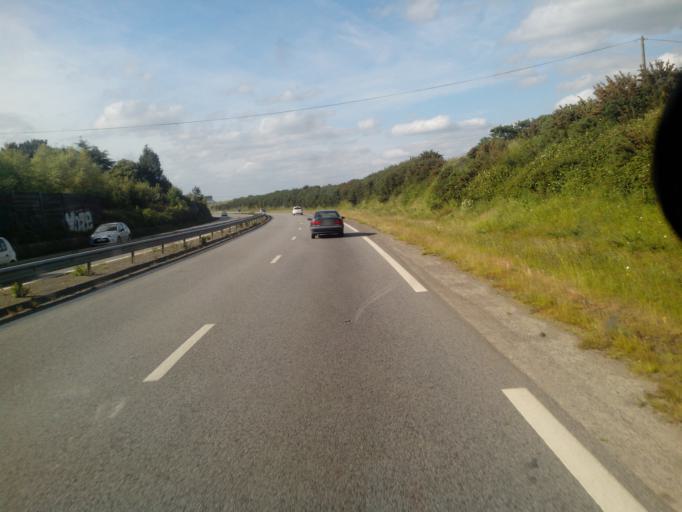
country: FR
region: Brittany
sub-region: Departement d'Ille-et-Vilaine
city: Cesson-Sevigne
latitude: 48.1456
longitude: -1.6250
